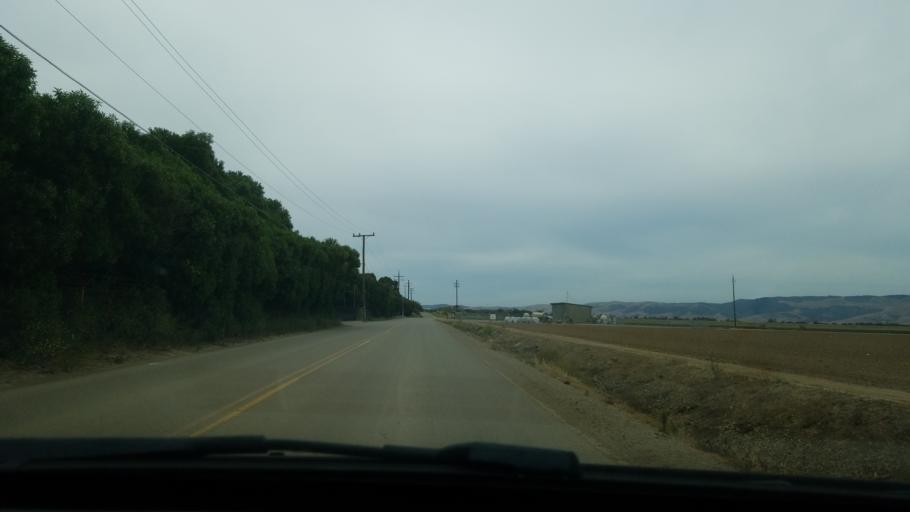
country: US
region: California
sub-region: Santa Barbara County
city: Guadalupe
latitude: 34.9914
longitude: -120.5140
